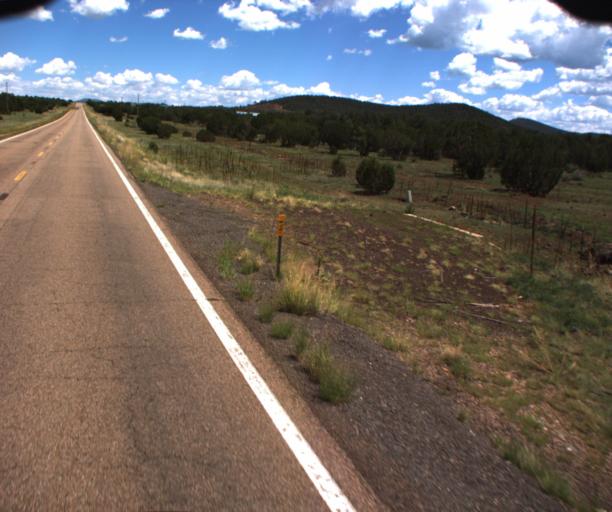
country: US
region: Arizona
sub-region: Navajo County
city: Pinetop-Lakeside
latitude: 34.2747
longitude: -109.7729
